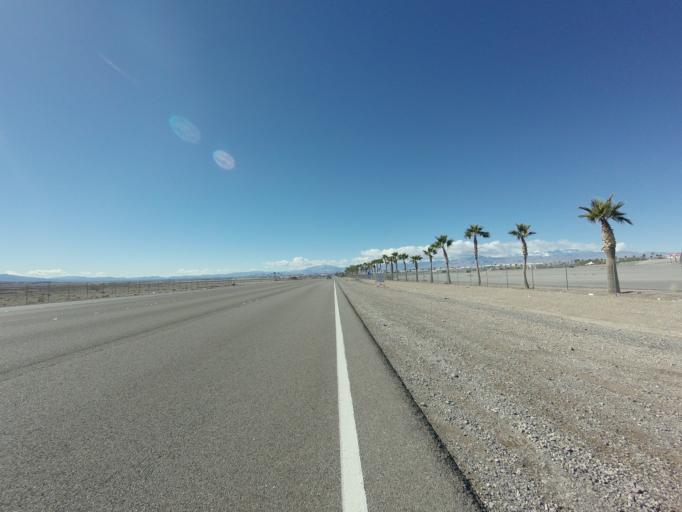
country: US
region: Nevada
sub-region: Clark County
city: Nellis Air Force Base
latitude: 36.2673
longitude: -115.0086
